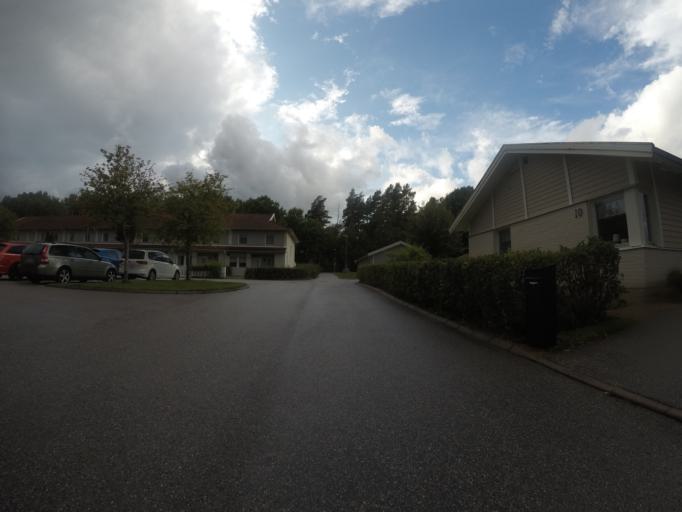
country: SE
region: Vaestmanland
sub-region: Vasteras
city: Vasteras
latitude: 59.6527
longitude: 16.5324
